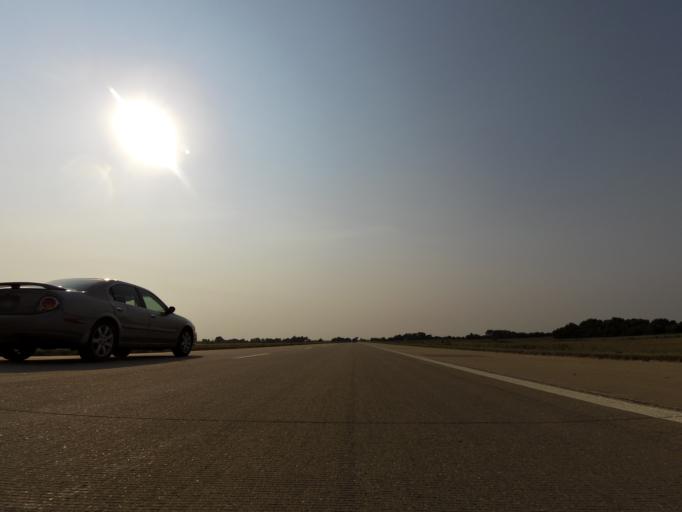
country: US
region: Kansas
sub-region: Sedgwick County
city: Colwich
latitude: 37.8501
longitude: -97.5987
